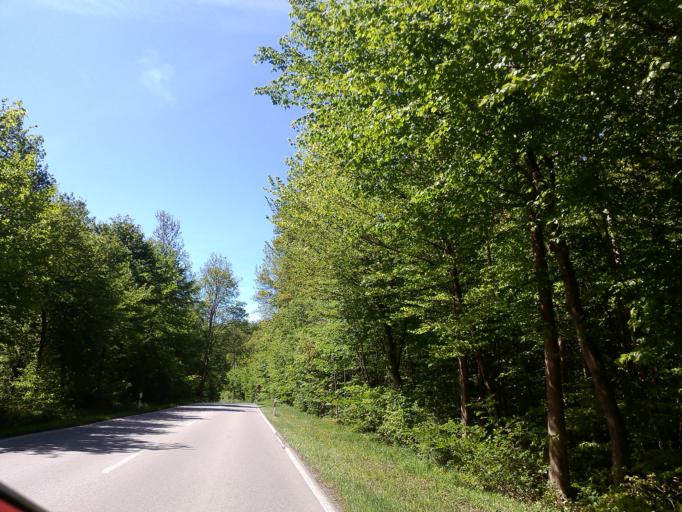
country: DE
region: Bavaria
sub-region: Upper Bavaria
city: Gauting
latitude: 48.0461
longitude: 11.3661
